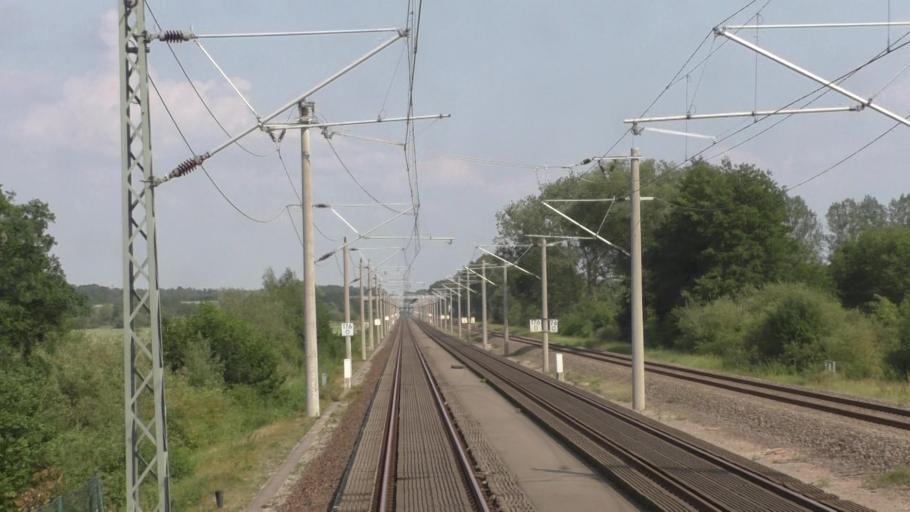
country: DE
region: Brandenburg
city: Rathenow
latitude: 52.5909
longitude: 12.2786
